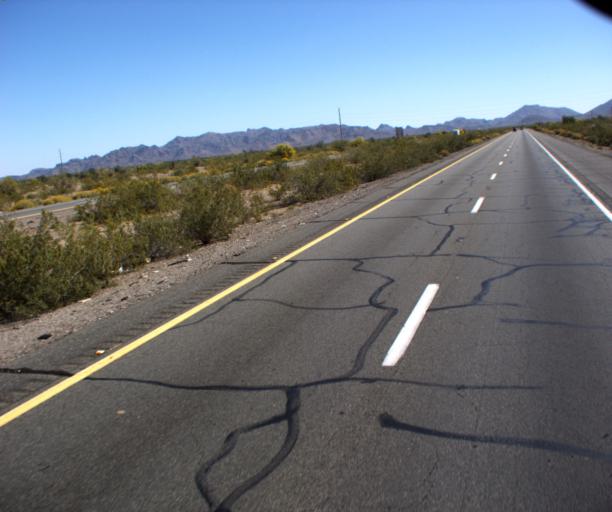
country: US
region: Arizona
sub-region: La Paz County
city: Quartzsite
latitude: 33.6687
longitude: -114.1699
